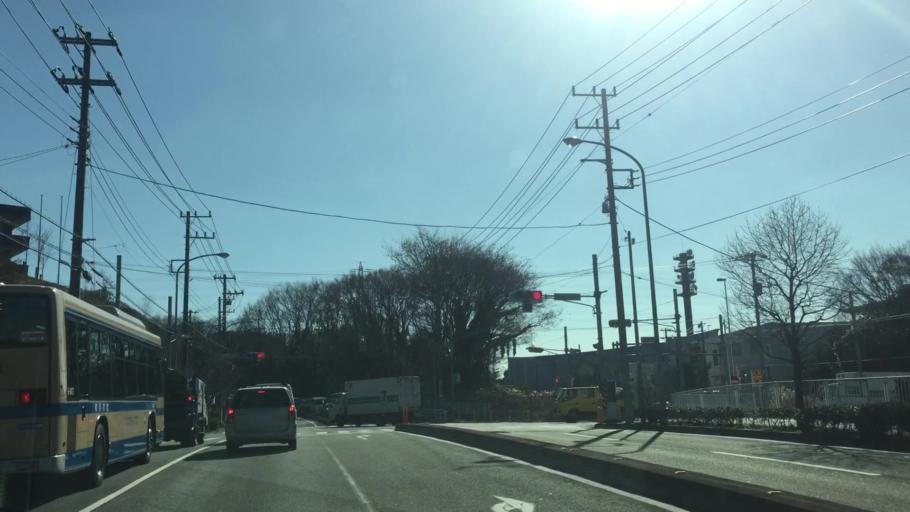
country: JP
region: Kanagawa
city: Yokohama
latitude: 35.4854
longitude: 139.5947
